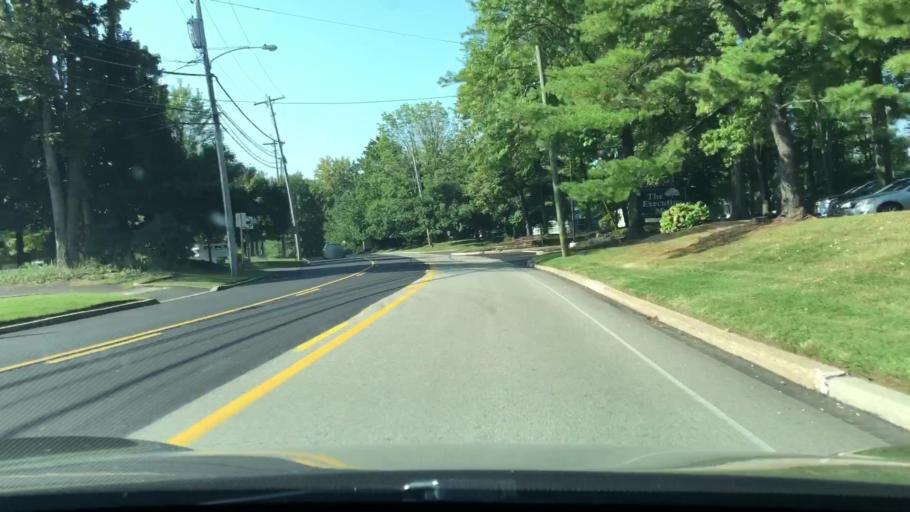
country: US
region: Pennsylvania
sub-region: Montgomery County
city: Horsham
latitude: 40.1593
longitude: -75.1351
